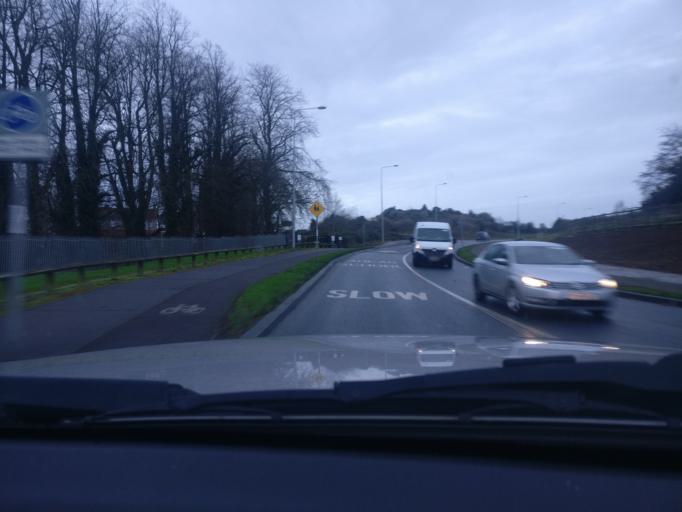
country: IE
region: Leinster
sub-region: An Mhi
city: Navan
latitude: 53.6543
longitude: -6.6985
